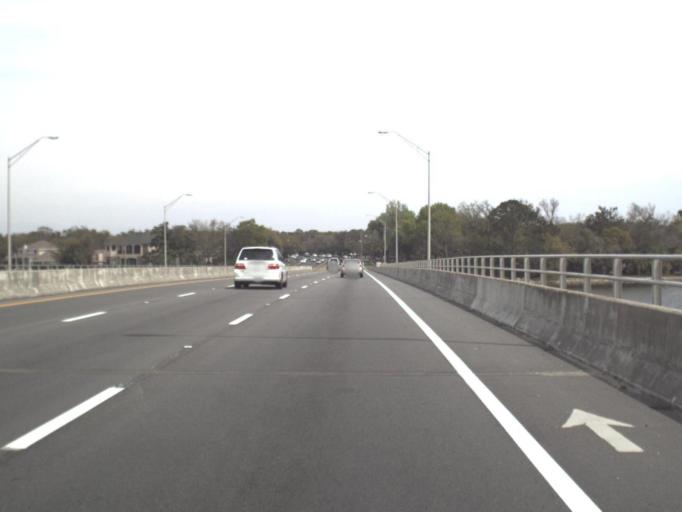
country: US
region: Florida
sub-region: Okaloosa County
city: Ocean City
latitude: 30.4403
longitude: -86.5898
